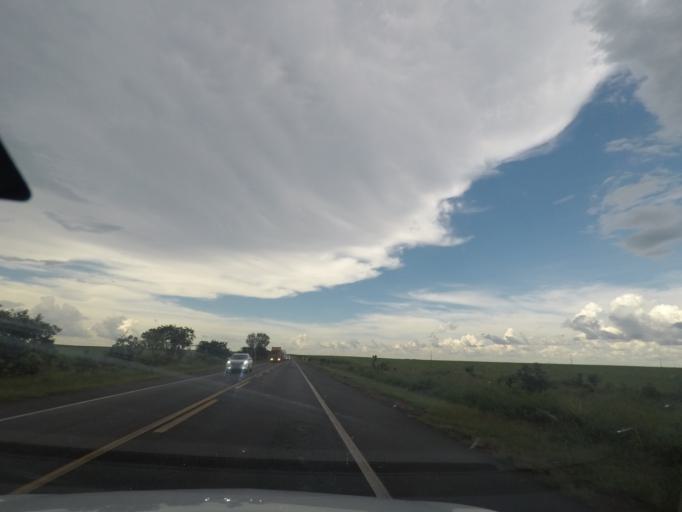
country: BR
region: Minas Gerais
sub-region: Prata
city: Prata
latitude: -19.6254
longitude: -48.8463
